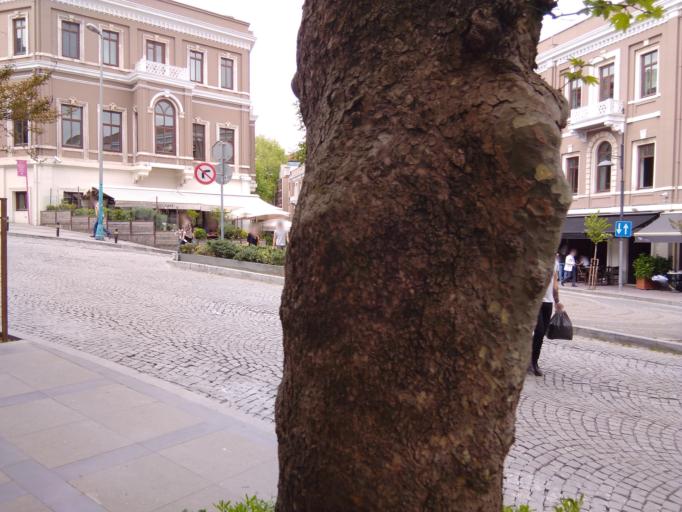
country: TR
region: Istanbul
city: Sisli
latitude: 41.0420
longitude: 29.0029
